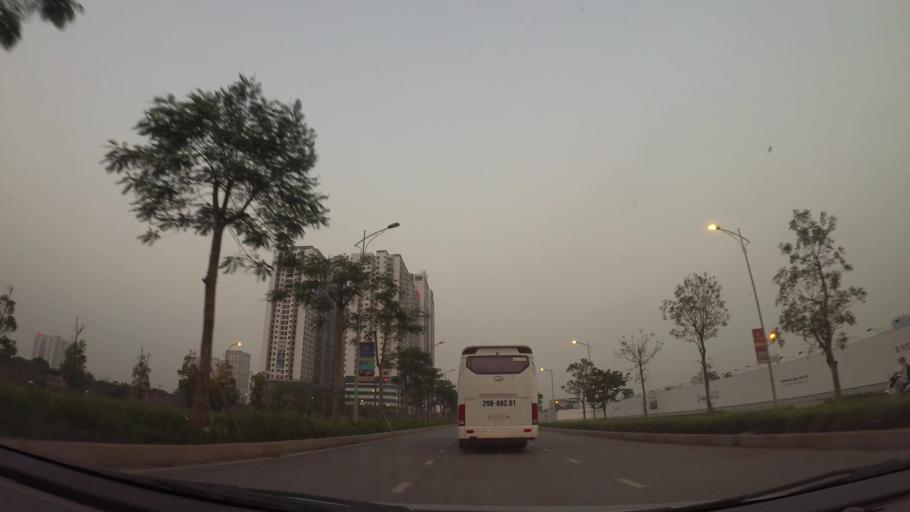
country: VN
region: Ha Noi
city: Tay Ho
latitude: 21.0625
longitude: 105.7919
